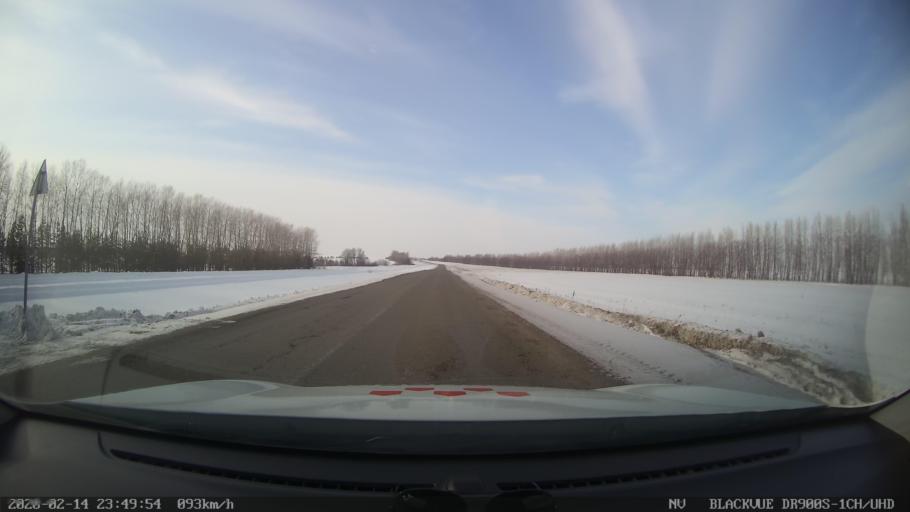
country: RU
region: Tatarstan
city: Kuybyshevskiy Zaton
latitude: 55.2567
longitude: 49.1718
